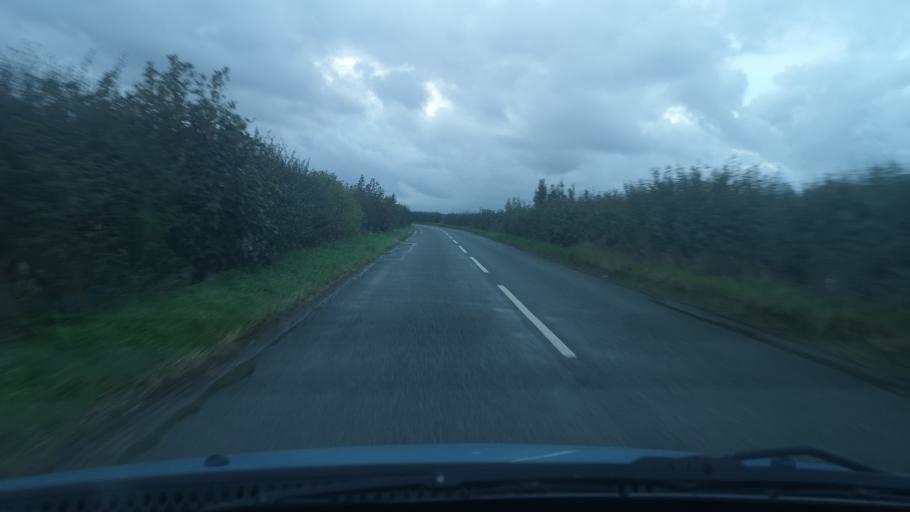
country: GB
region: England
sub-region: Doncaster
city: Norton
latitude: 53.6325
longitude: -1.1944
